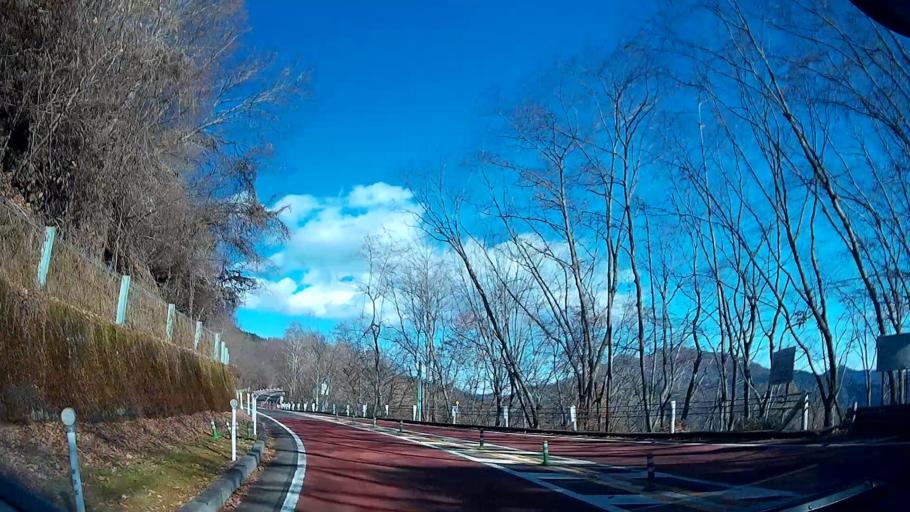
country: JP
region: Yamanashi
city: Uenohara
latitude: 35.7533
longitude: 139.0420
